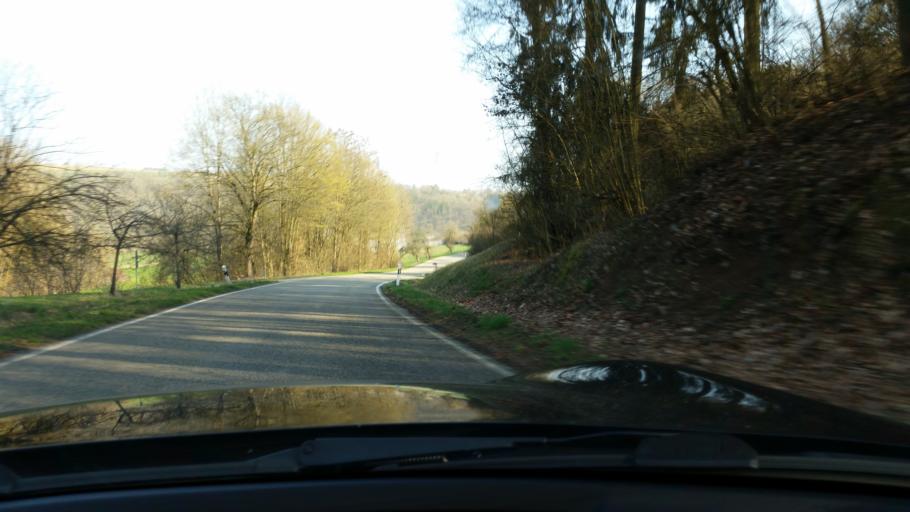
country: DE
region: Baden-Wuerttemberg
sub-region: Regierungsbezirk Stuttgart
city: Mockmuhl
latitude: 49.3325
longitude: 9.3435
